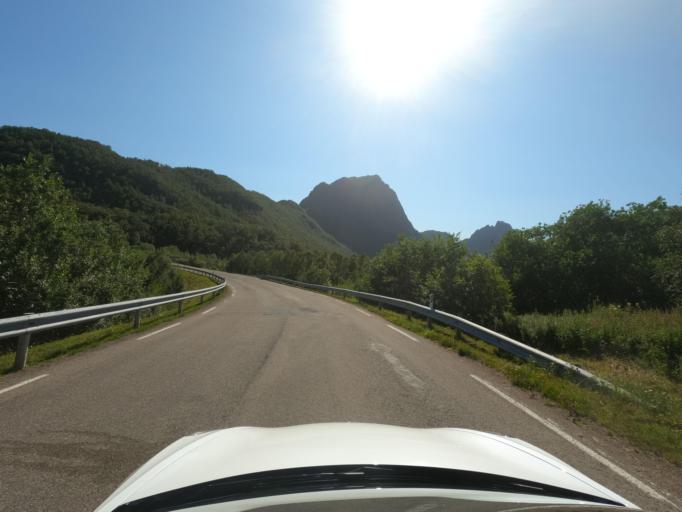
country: NO
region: Nordland
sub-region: Hadsel
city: Melbu
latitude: 68.4281
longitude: 14.8197
